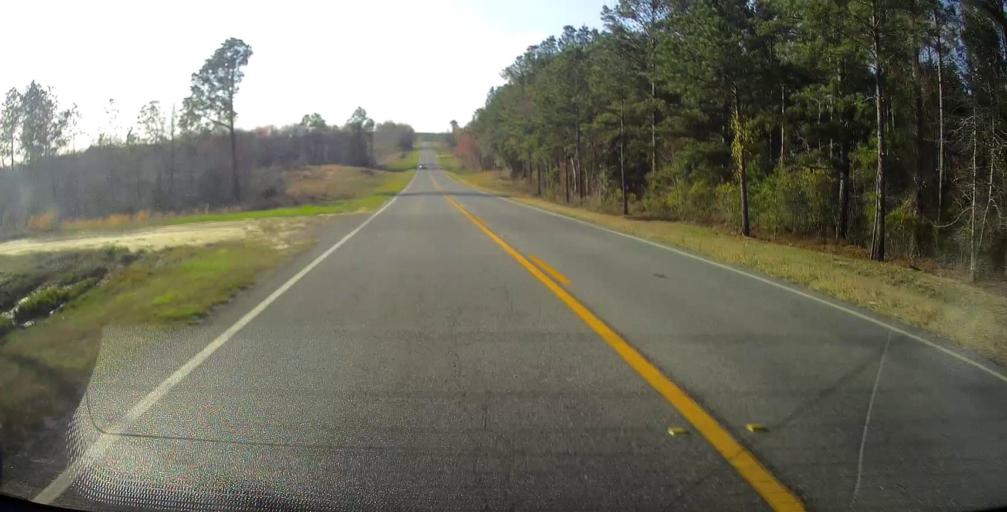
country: US
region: Georgia
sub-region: Tattnall County
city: Reidsville
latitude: 32.1301
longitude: -82.2167
